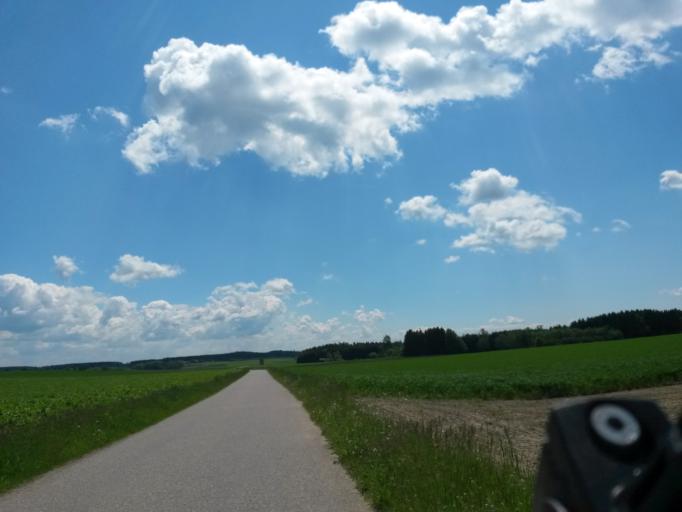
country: DE
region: Baden-Wuerttemberg
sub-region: Tuebingen Region
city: Ingoldingen
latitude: 47.9805
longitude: 9.7134
